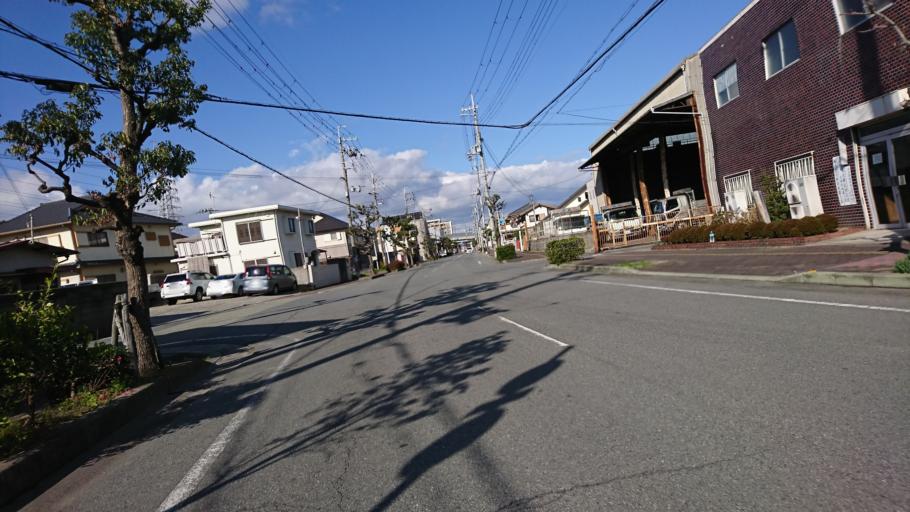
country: JP
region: Hyogo
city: Kakogawacho-honmachi
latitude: 34.7550
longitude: 134.7978
